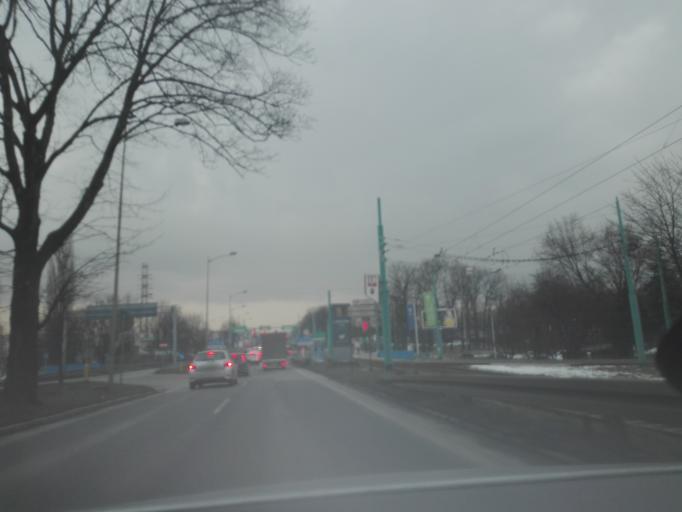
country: PL
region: Silesian Voivodeship
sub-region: Chorzow
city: Chorzow
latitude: 50.2868
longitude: 18.9689
